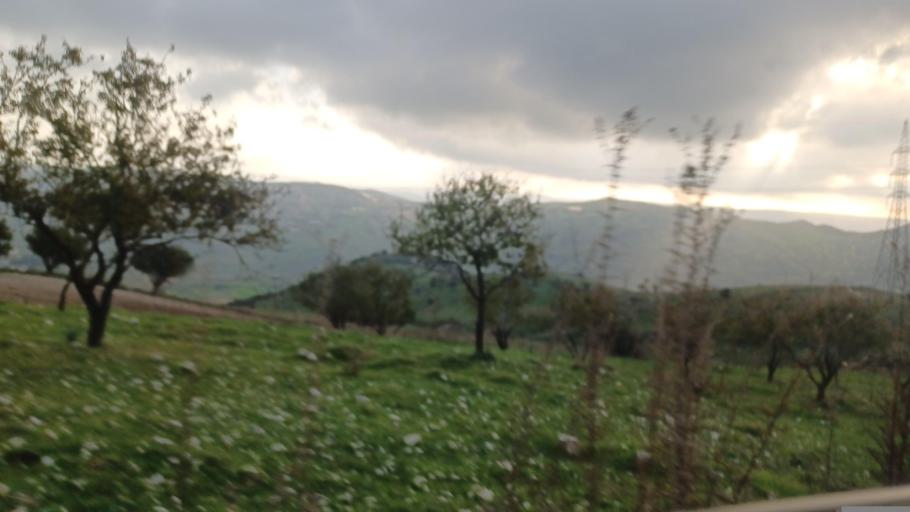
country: CY
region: Pafos
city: Mesogi
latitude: 34.7860
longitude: 32.5104
